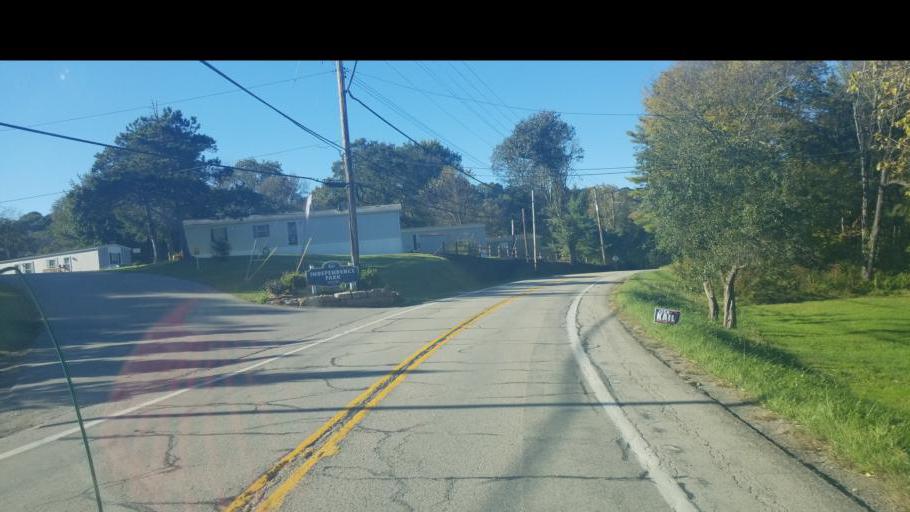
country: US
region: Pennsylvania
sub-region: Washington County
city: Burgettstown
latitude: 40.4978
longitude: -80.3626
